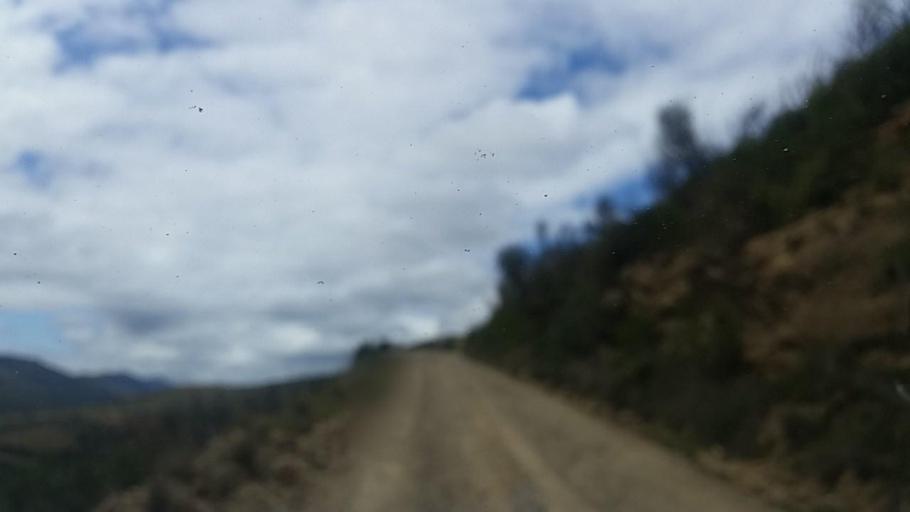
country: ZA
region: Western Cape
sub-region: Eden District Municipality
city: Knysna
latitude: -33.8220
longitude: 23.1787
